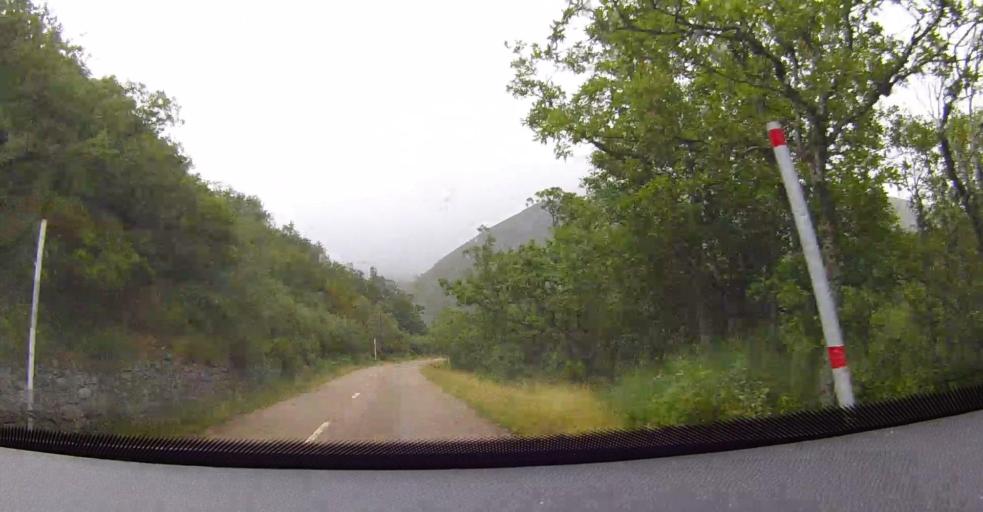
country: ES
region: Castille and Leon
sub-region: Provincia de Leon
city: Puebla de Lillo
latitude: 43.0703
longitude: -5.2657
